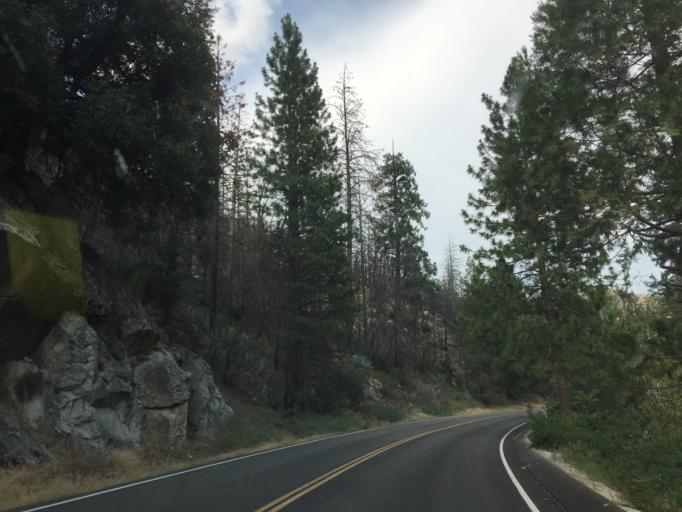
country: US
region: California
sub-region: Tulare County
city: Three Rivers
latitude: 36.8035
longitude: -118.7061
